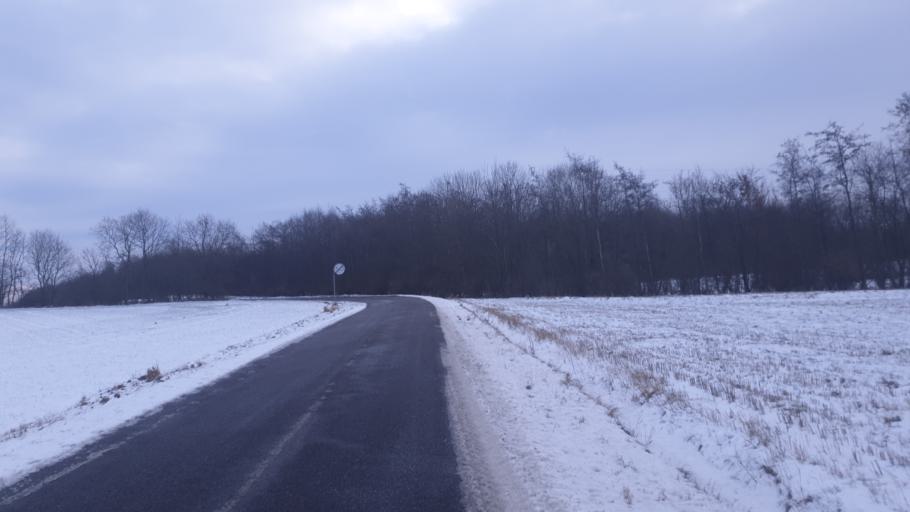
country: DK
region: Central Jutland
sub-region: Hedensted Kommune
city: Hedensted
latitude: 55.7934
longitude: 9.7147
